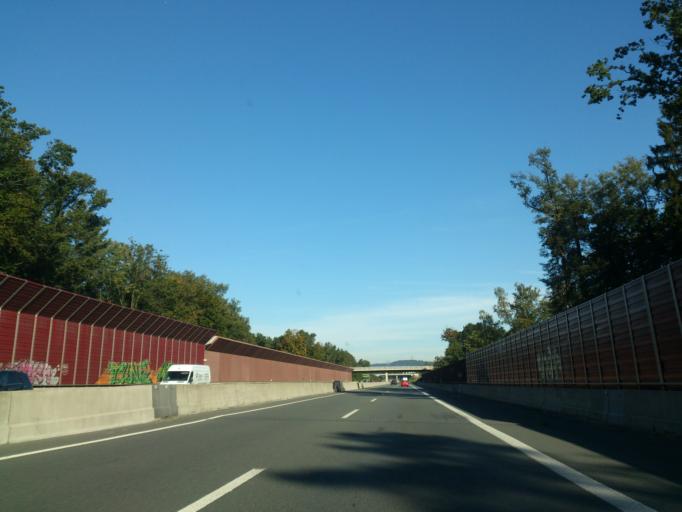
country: DE
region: North Rhine-Westphalia
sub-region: Regierungsbezirk Detmold
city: Verl
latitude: 51.9530
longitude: 8.5057
